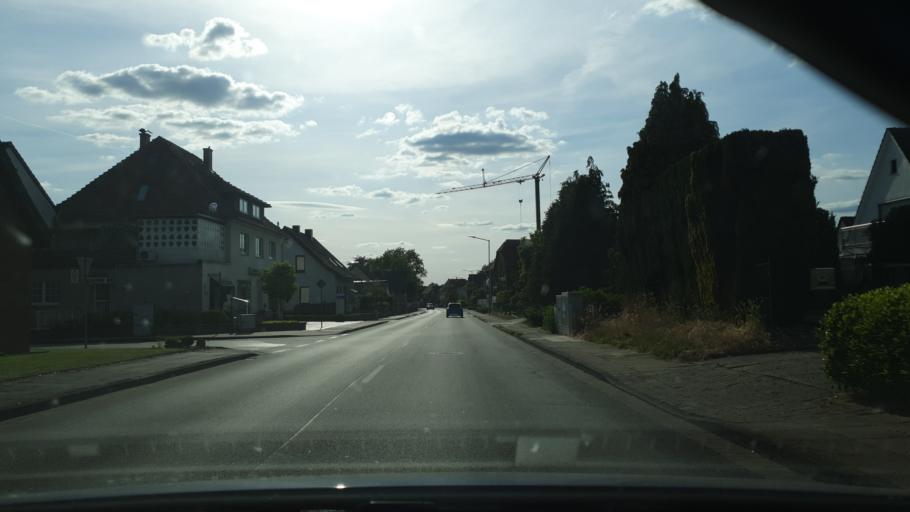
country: DE
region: North Rhine-Westphalia
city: Spenge
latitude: 52.1405
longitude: 8.5028
